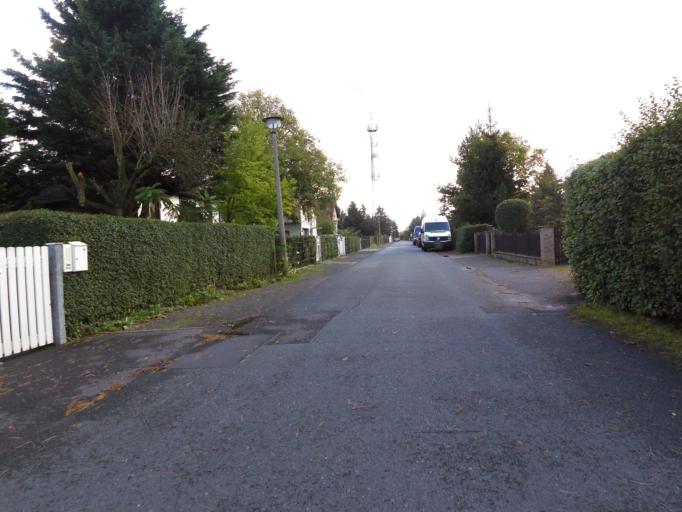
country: DE
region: Saxony
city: Grossposna
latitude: 51.3201
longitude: 12.4744
